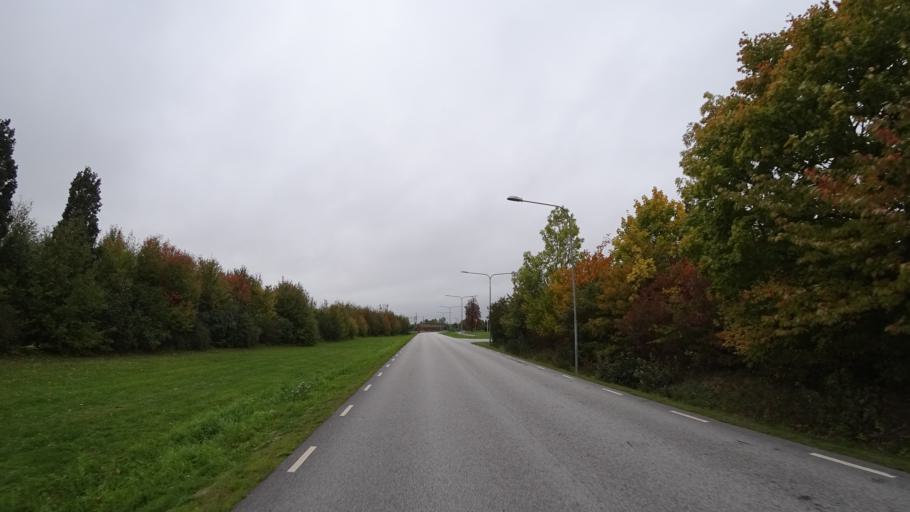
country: SE
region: Skane
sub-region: Kavlinge Kommun
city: Kaevlinge
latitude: 55.7991
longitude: 13.1117
